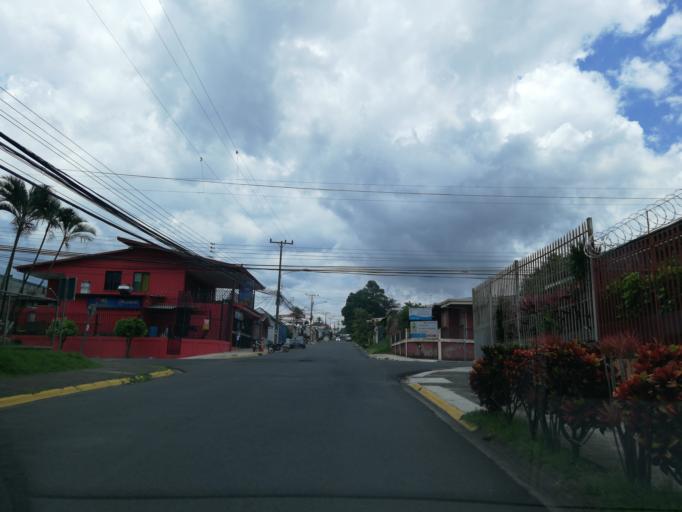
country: CR
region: Alajuela
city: Alajuela
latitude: 10.0125
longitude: -84.2278
